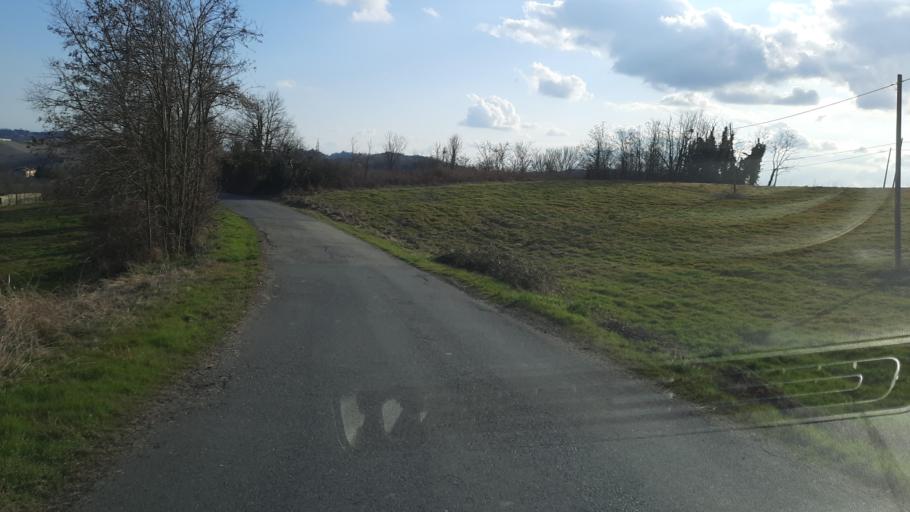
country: IT
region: Piedmont
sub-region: Provincia di Alessandria
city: Ozzano Monferrato
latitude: 45.1145
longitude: 8.3825
